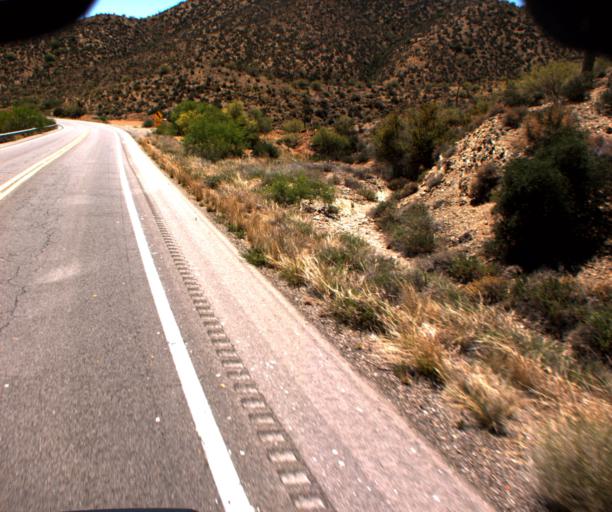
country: US
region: Arizona
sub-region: Pinal County
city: Superior
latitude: 33.1738
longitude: -111.0171
